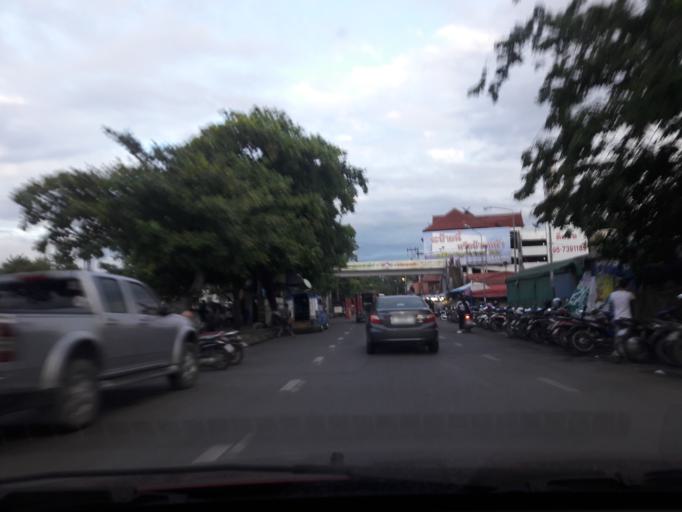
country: TH
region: Chiang Mai
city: Chiang Mai
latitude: 18.7916
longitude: 99.0007
